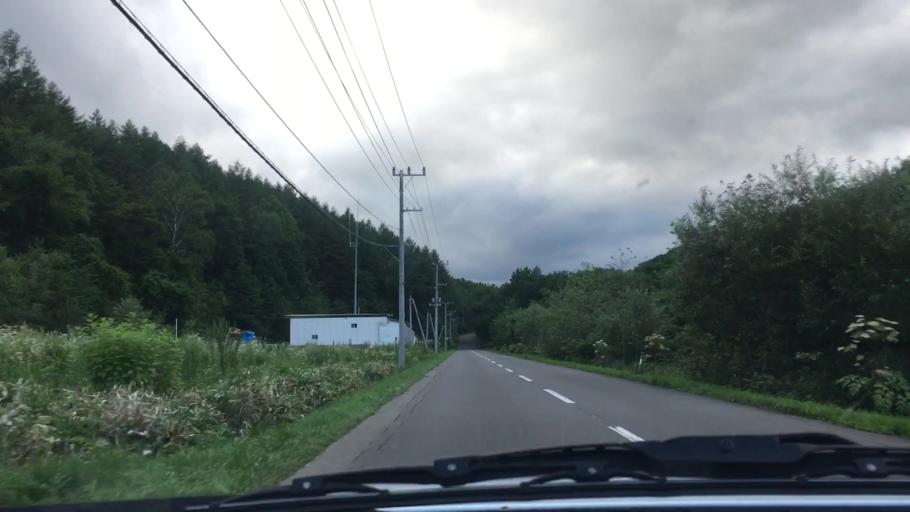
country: JP
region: Hokkaido
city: Otofuke
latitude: 43.1430
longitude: 142.8812
